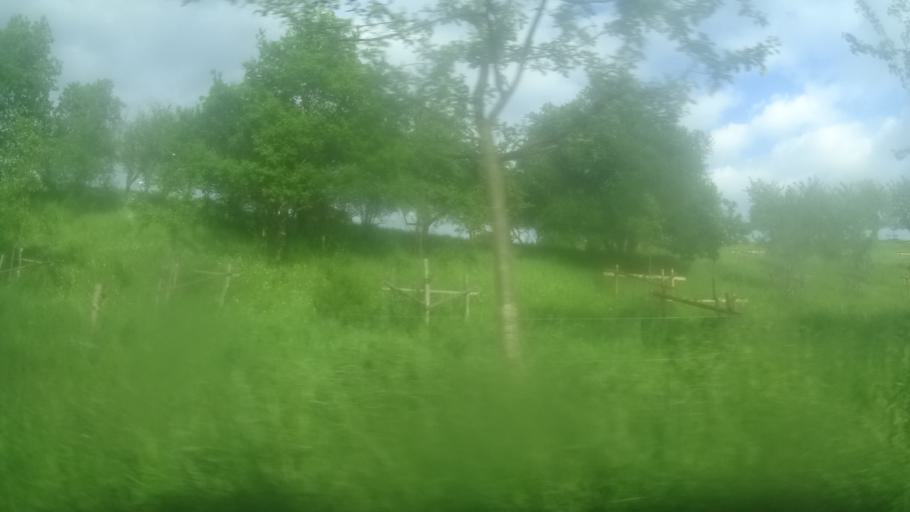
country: DE
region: Thuringia
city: Saalfeld
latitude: 50.6935
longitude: 11.3817
